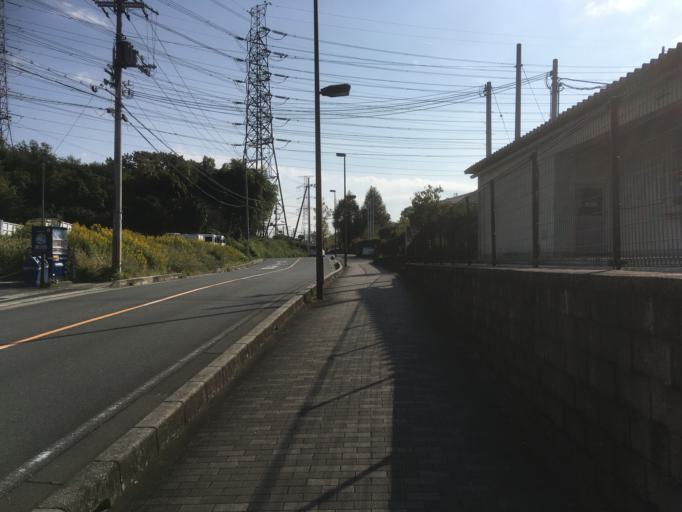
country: JP
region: Nara
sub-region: Ikoma-shi
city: Ikoma
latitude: 34.7308
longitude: 135.7139
